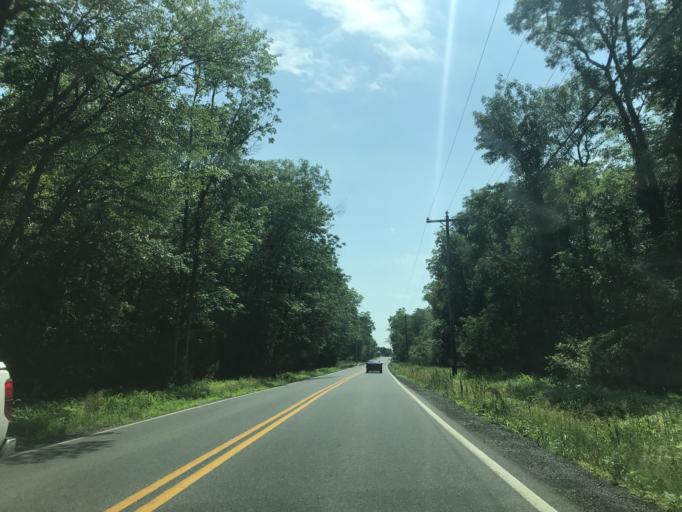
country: US
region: Maryland
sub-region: Dorchester County
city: Hurlock
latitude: 38.5802
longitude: -75.7911
